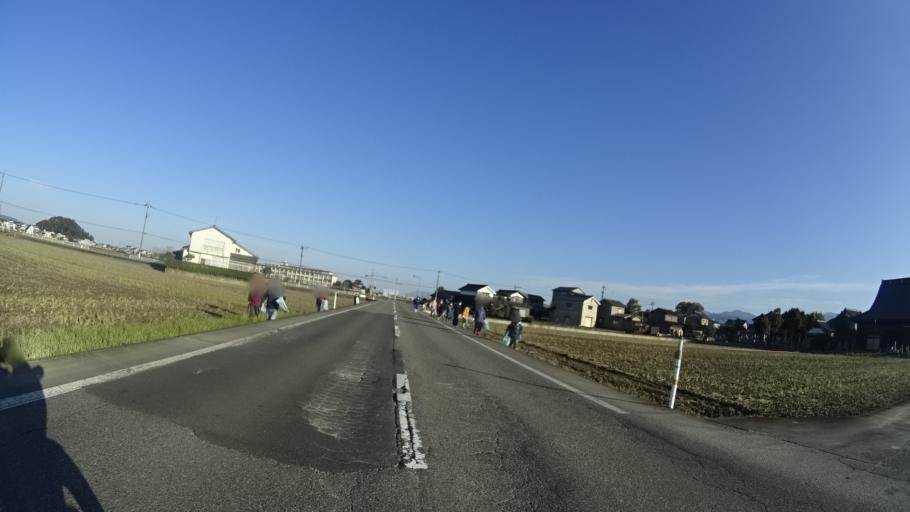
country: JP
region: Fukui
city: Fukui-shi
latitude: 36.0698
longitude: 136.2569
